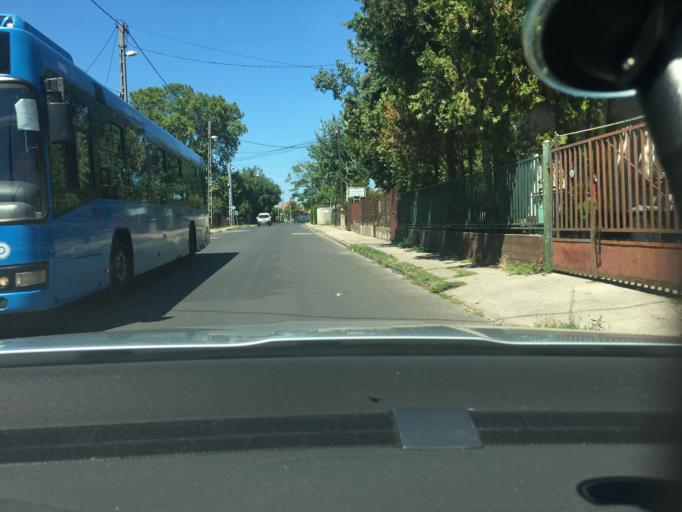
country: HU
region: Budapest
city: Budapest XVI. keruelet
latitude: 47.5136
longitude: 19.1656
